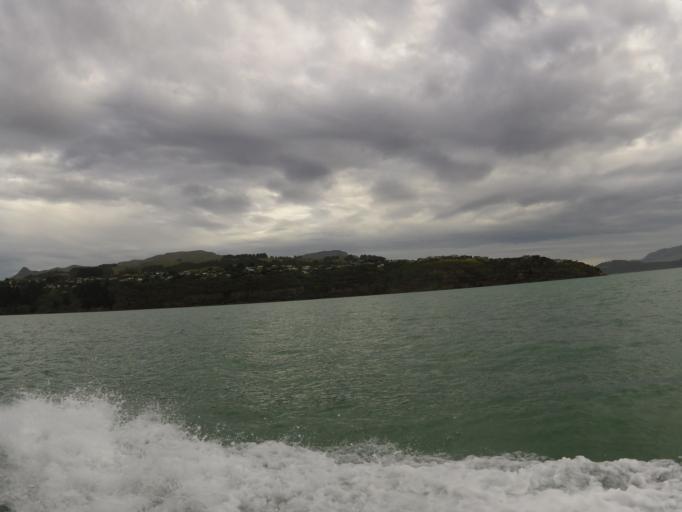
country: NZ
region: Canterbury
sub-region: Christchurch City
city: Christchurch
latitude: -43.6181
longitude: 172.7270
